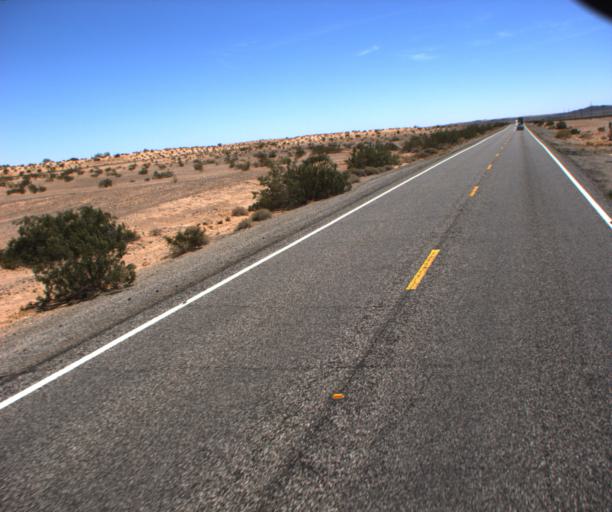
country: US
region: Arizona
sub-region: La Paz County
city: Parker
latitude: 34.0467
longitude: -114.2581
